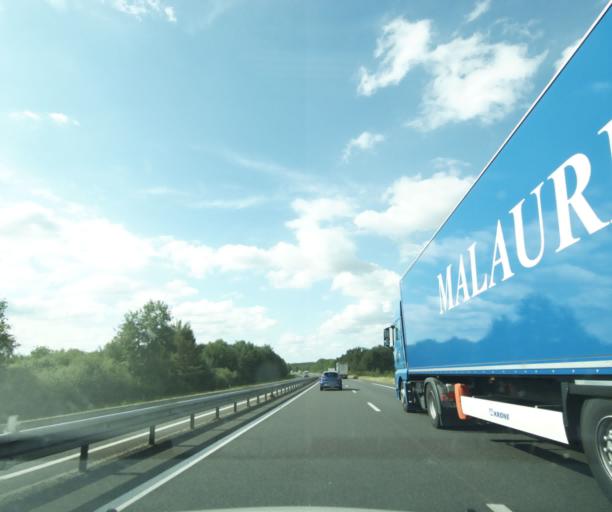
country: FR
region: Centre
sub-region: Departement du Loiret
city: La Ferte-Saint-Aubin
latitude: 47.7096
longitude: 1.9005
